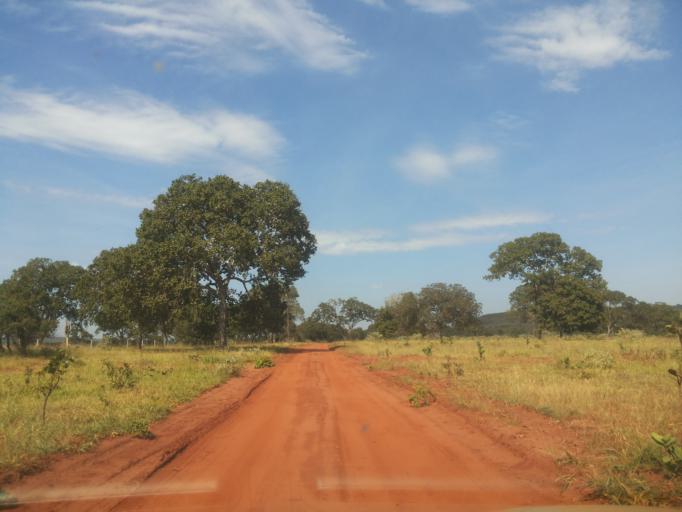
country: BR
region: Minas Gerais
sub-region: Ituiutaba
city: Ituiutaba
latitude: -19.0603
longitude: -49.3642
